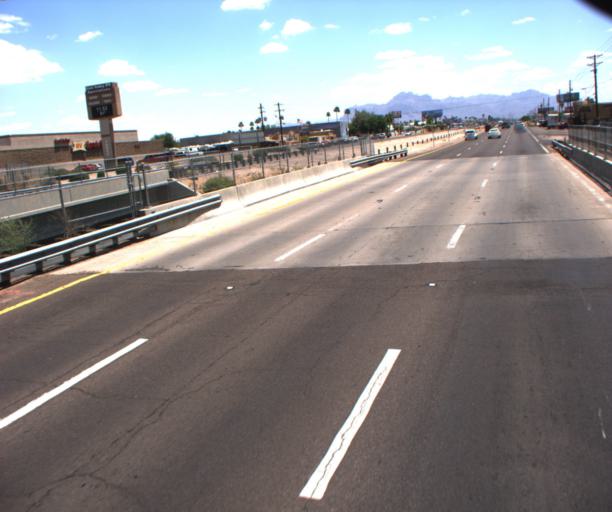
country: US
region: Arizona
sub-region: Pinal County
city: Apache Junction
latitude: 33.4151
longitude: -111.6145
